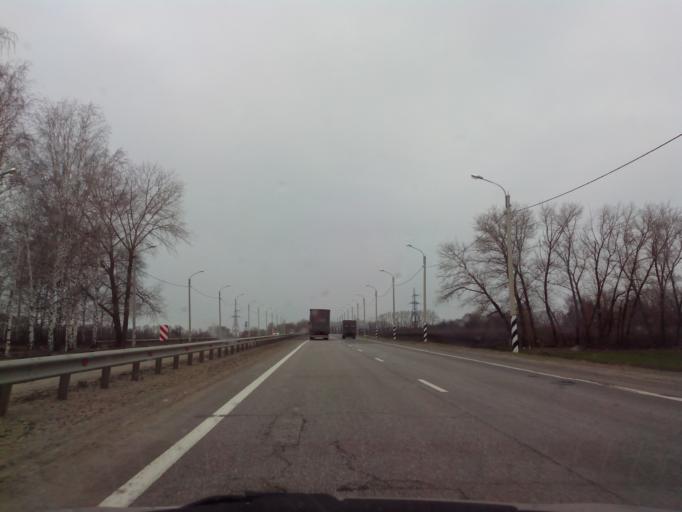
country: RU
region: Tambov
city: Selezni
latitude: 52.7496
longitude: 41.1853
